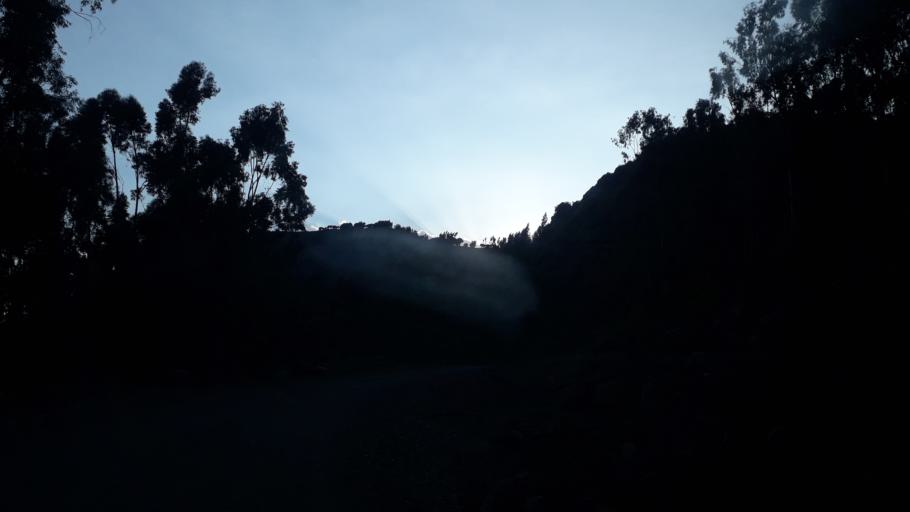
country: ET
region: Amhara
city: Lalibela
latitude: 11.5516
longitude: 39.2161
